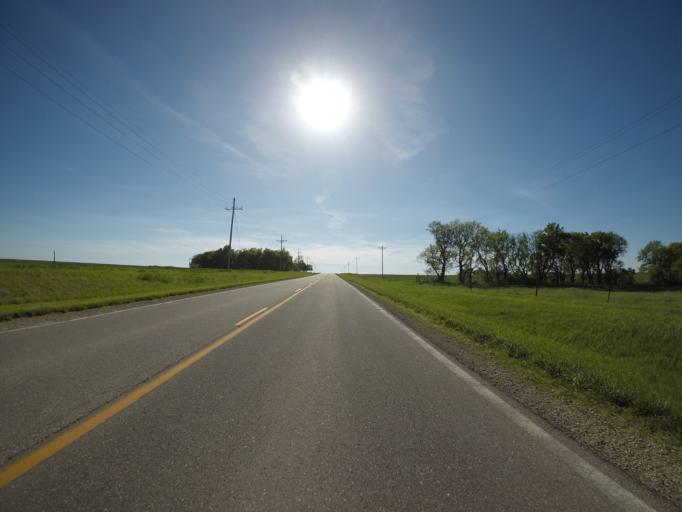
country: US
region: Kansas
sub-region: Clay County
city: Clay Center
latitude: 39.3646
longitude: -96.8770
